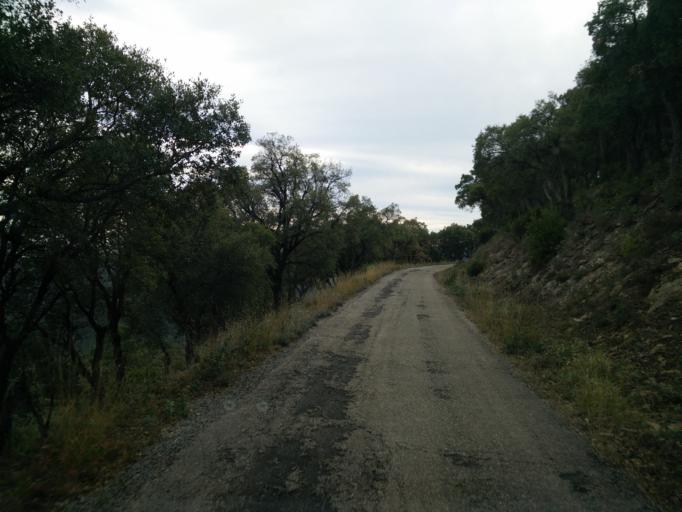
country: FR
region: Provence-Alpes-Cote d'Azur
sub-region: Departement du Var
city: Roquebrune-sur-Argens
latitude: 43.3994
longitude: 6.6202
